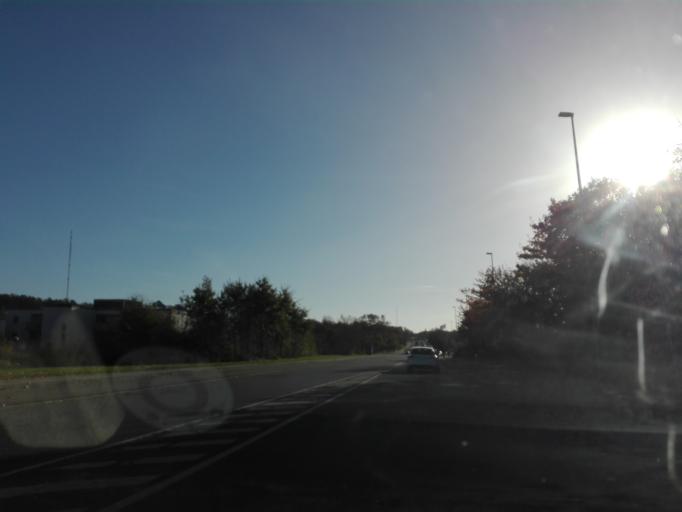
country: DK
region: Central Jutland
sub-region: Arhus Kommune
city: Arhus
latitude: 56.1093
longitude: 10.2082
